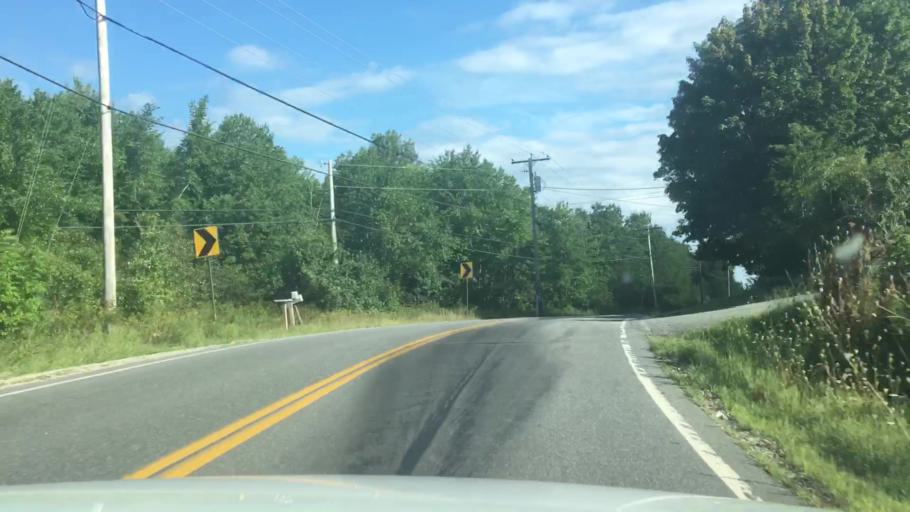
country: US
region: Maine
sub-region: Androscoggin County
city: Lisbon Falls
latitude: 43.9712
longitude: -70.0618
